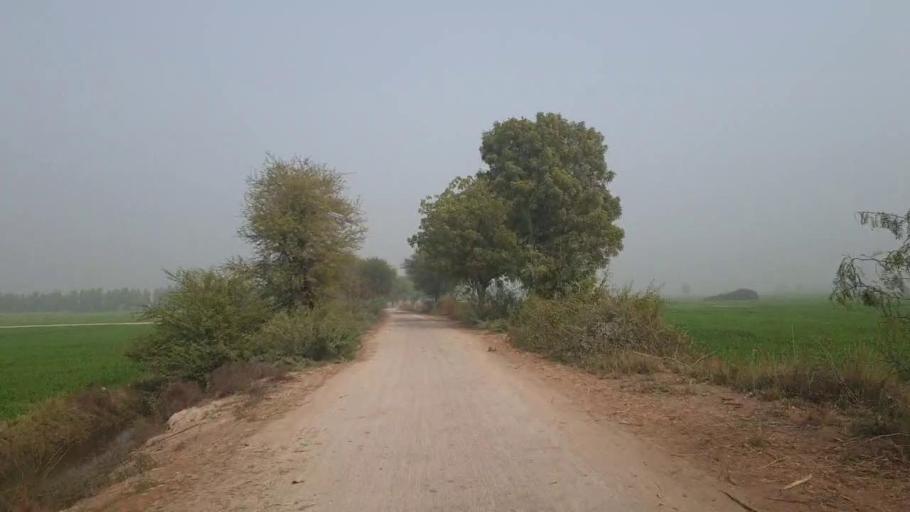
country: PK
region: Sindh
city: Bhit Shah
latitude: 25.8085
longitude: 68.5570
